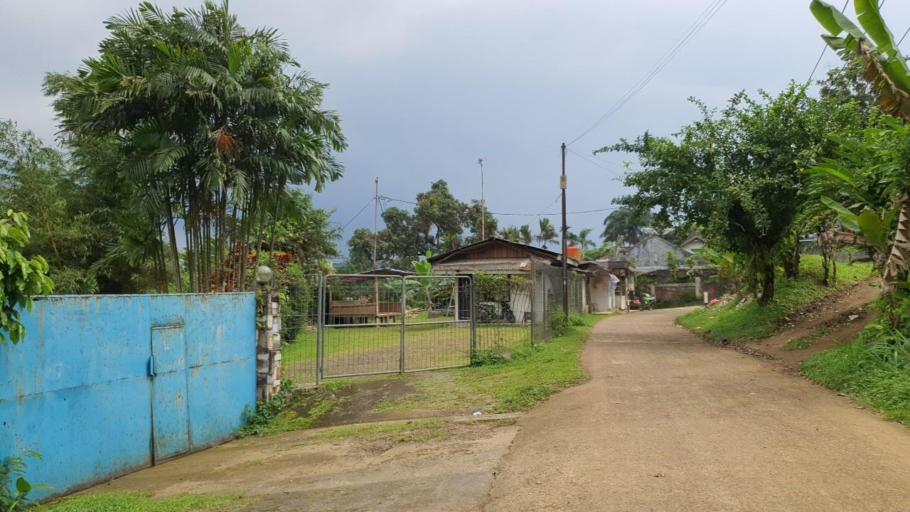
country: ID
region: West Java
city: Caringin
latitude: -6.6527
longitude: 106.8850
